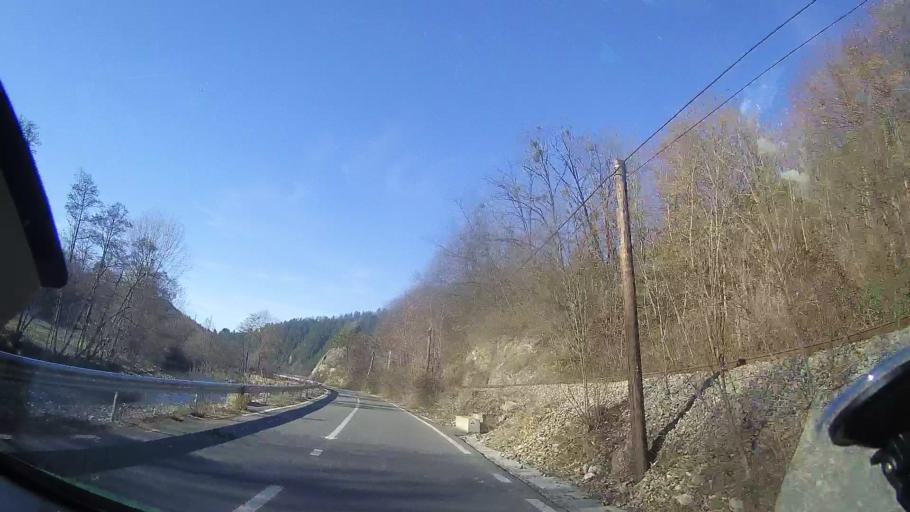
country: RO
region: Bihor
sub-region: Comuna Bratca
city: Bratca
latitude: 46.9295
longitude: 22.6427
